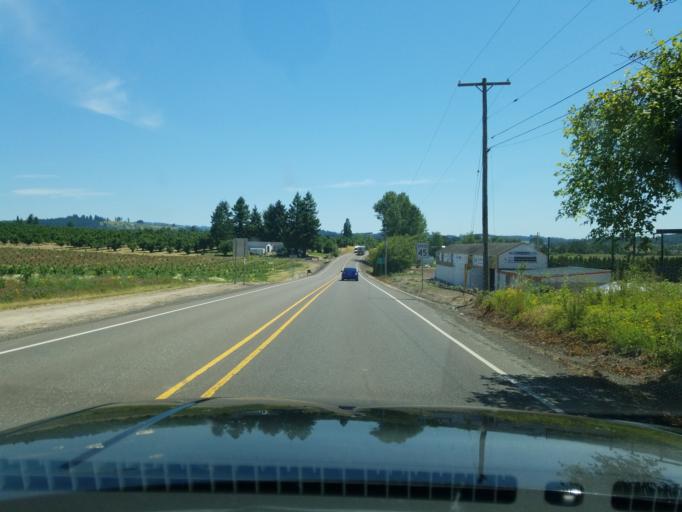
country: US
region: Oregon
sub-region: Yamhill County
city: Yamhill
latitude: 45.3459
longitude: -123.1864
